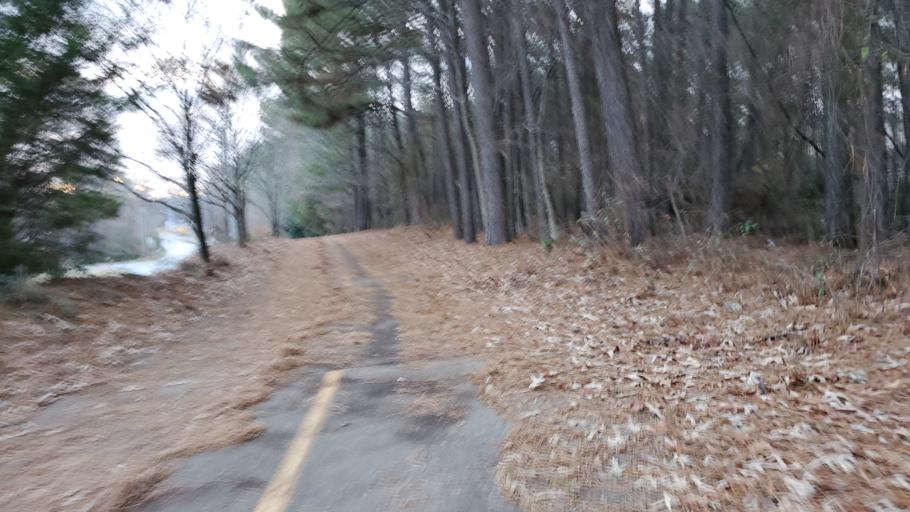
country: US
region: Georgia
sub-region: DeKalb County
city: Clarkston
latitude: 33.8184
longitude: -84.2307
